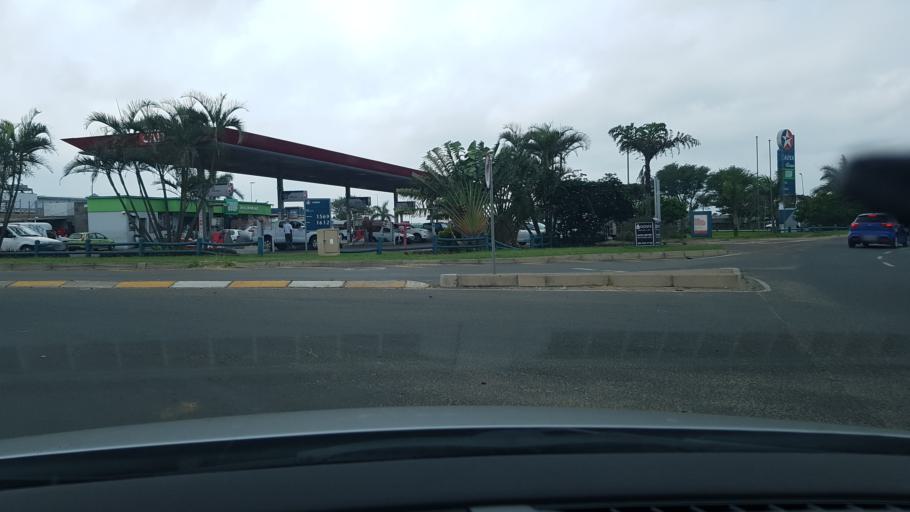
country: ZA
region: KwaZulu-Natal
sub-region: uThungulu District Municipality
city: Richards Bay
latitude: -28.7487
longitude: 32.0528
